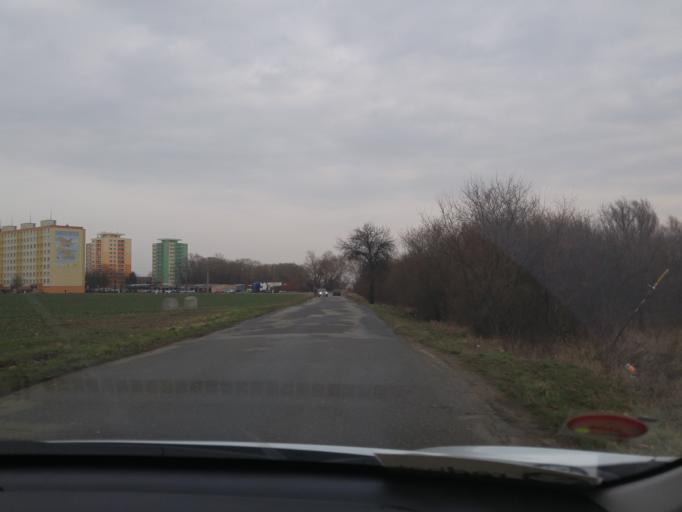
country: CZ
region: Central Bohemia
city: Neratovice
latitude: 50.2475
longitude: 14.5161
